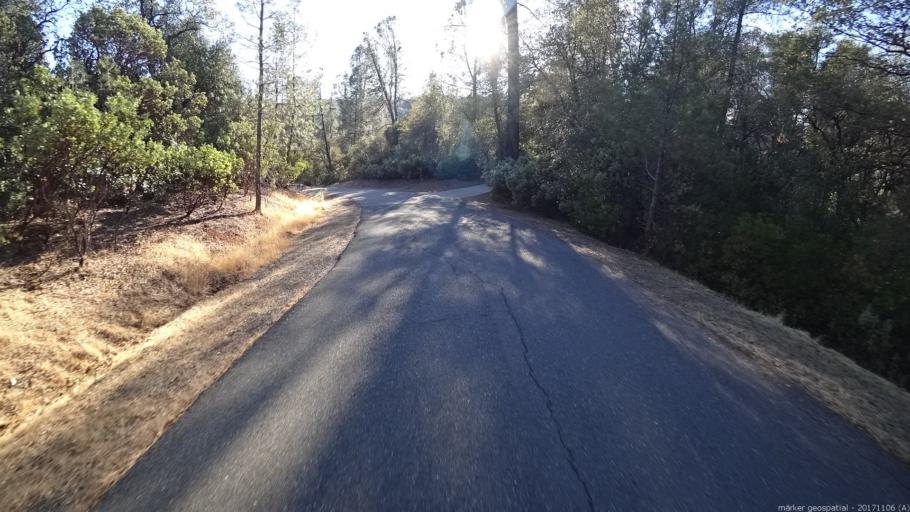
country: US
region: California
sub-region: Shasta County
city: Shasta
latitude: 40.5833
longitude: -122.4793
